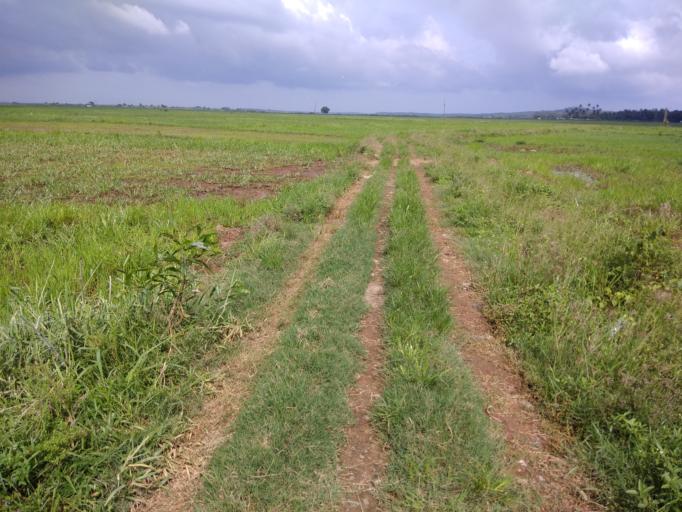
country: IN
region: Kerala
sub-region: Thrissur District
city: Trichur
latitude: 10.5390
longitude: 76.1779
